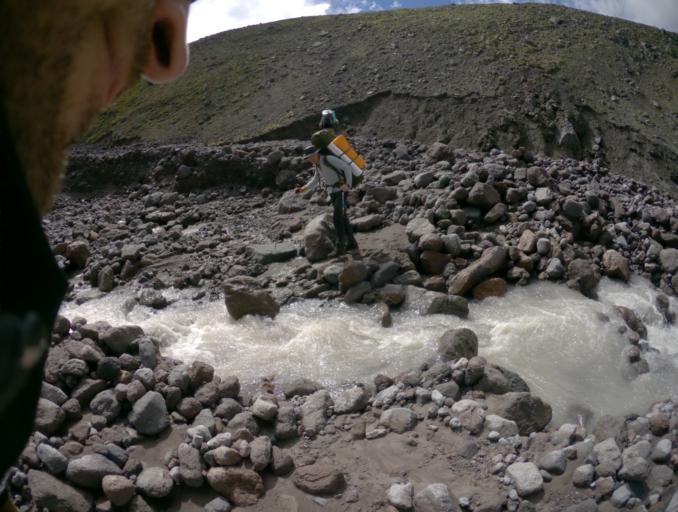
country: RU
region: Kabardino-Balkariya
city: Terskol
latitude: 43.3855
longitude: 42.3653
